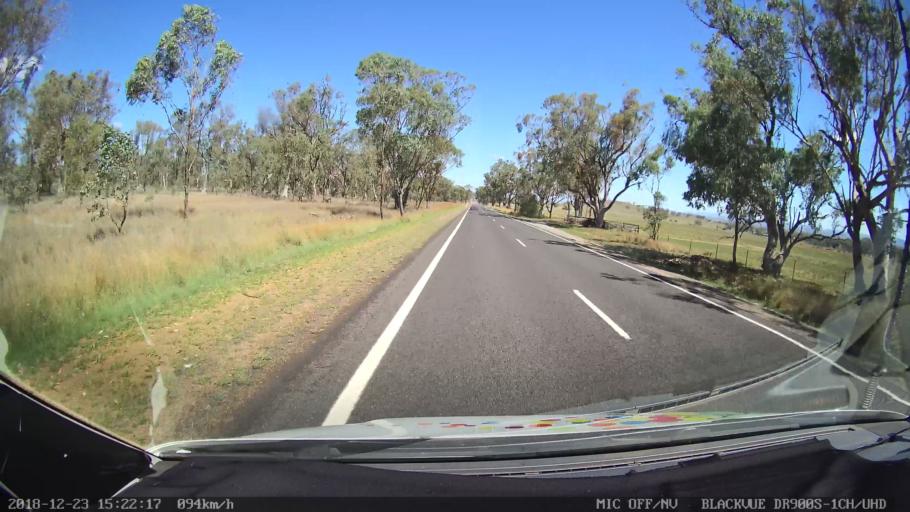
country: AU
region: New South Wales
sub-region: Tamworth Municipality
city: Manilla
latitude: -30.8664
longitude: 150.8034
